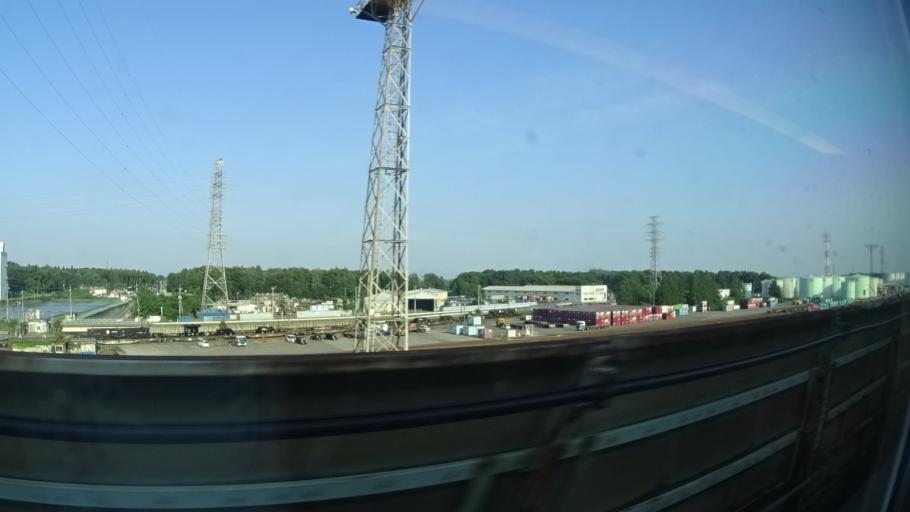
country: JP
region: Tochigi
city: Kaminokawa
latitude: 36.4520
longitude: 139.8695
